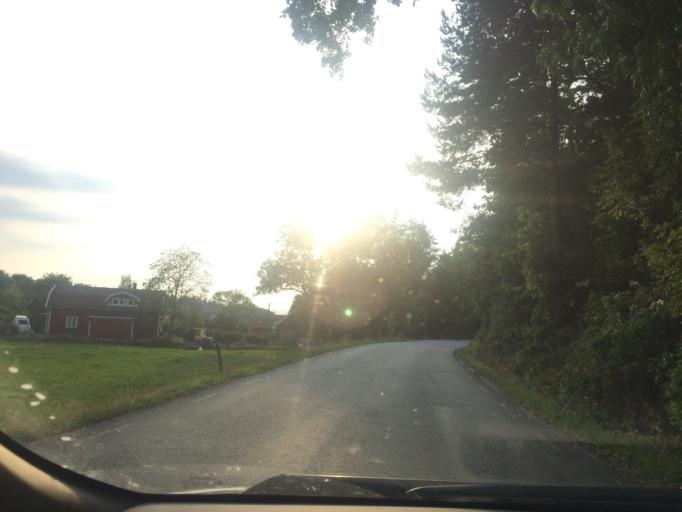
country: SE
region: Vaestra Goetaland
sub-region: Alingsas Kommun
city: Alingsas
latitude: 58.0129
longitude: 12.5502
